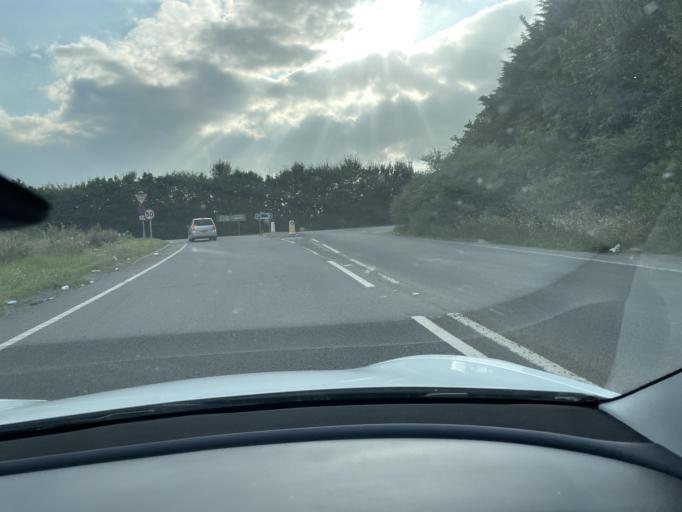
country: GB
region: England
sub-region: Northamptonshire
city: Long Buckby
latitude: 52.3982
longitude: -1.0321
